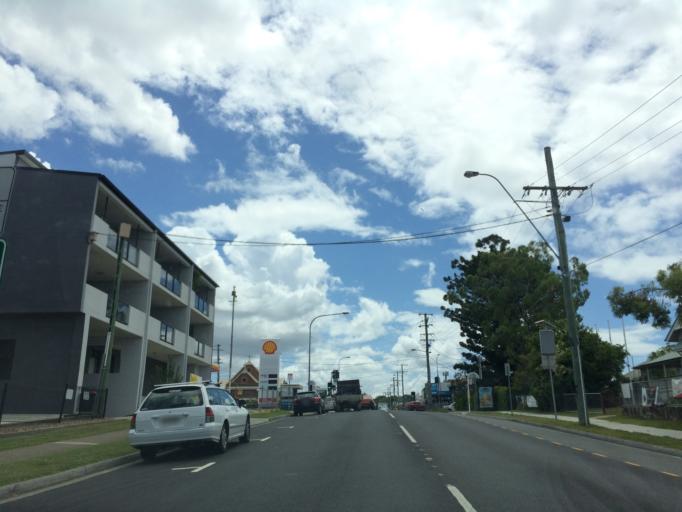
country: AU
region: Queensland
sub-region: Brisbane
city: Rocklea
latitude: -27.5326
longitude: 152.9842
